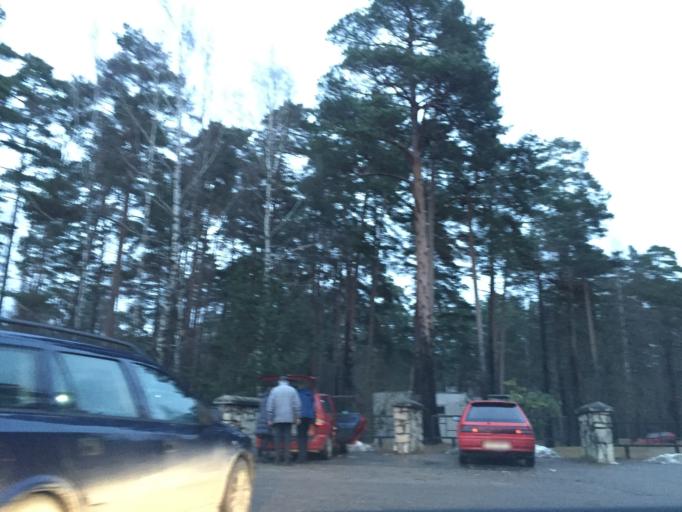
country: LV
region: Riga
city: Jaunciems
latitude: 57.0416
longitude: 24.1897
